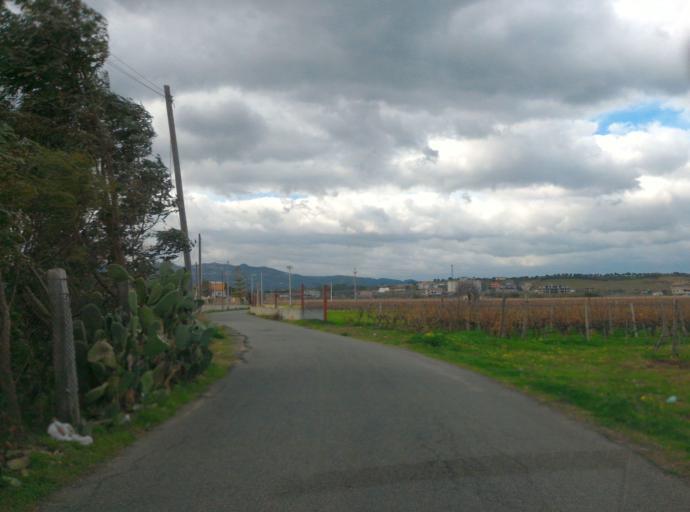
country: IT
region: Calabria
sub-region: Provincia di Crotone
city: Ciro Marina
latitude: 39.3908
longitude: 17.1367
